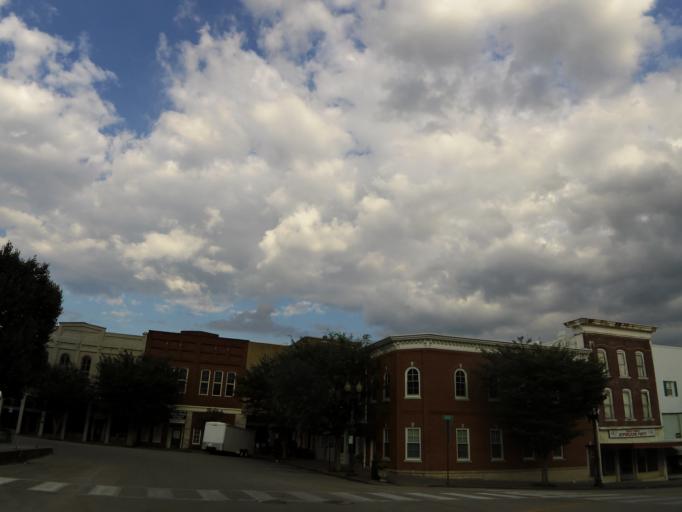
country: US
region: Tennessee
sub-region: Maury County
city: Columbia
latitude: 35.6146
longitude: -87.0341
